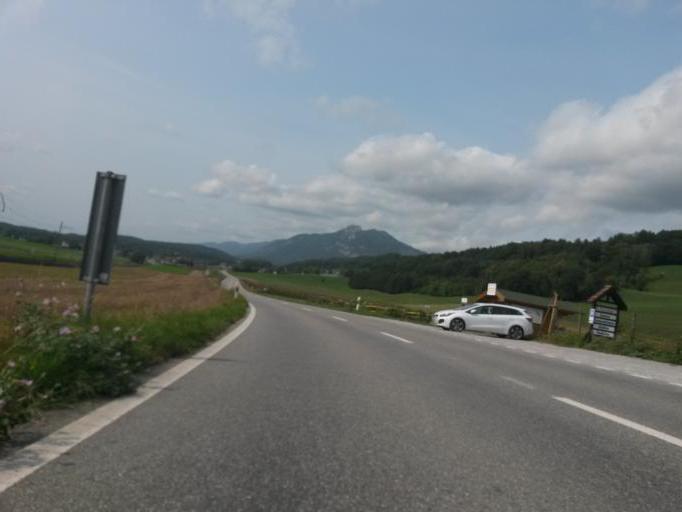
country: CH
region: Bern
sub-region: Oberaargau
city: Wiedlisbach
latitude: 47.2497
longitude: 7.6307
